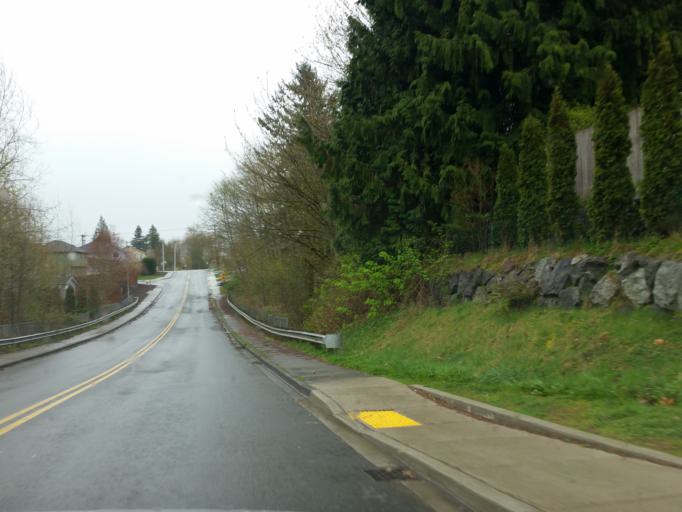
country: US
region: Washington
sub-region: Snohomish County
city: Silver Firs
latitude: 47.8906
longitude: -122.1668
